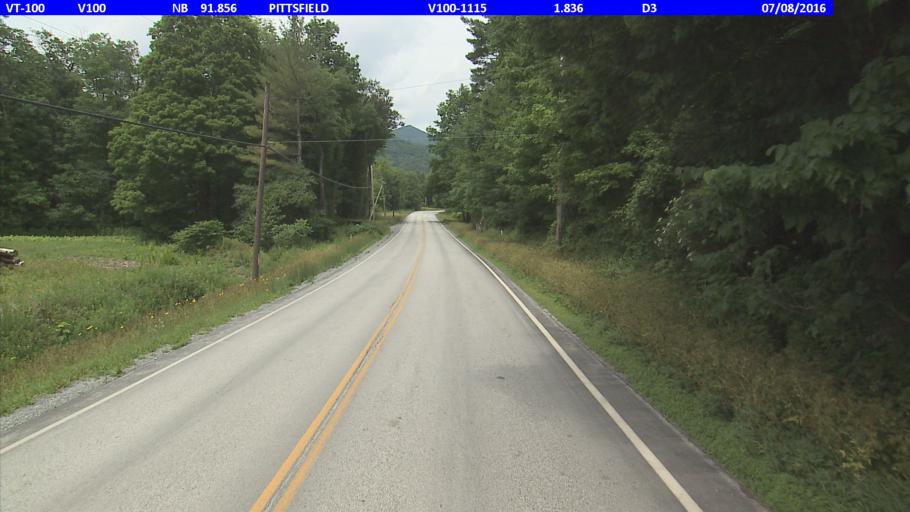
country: US
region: Vermont
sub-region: Rutland County
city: Rutland
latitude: 43.7435
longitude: -72.8200
